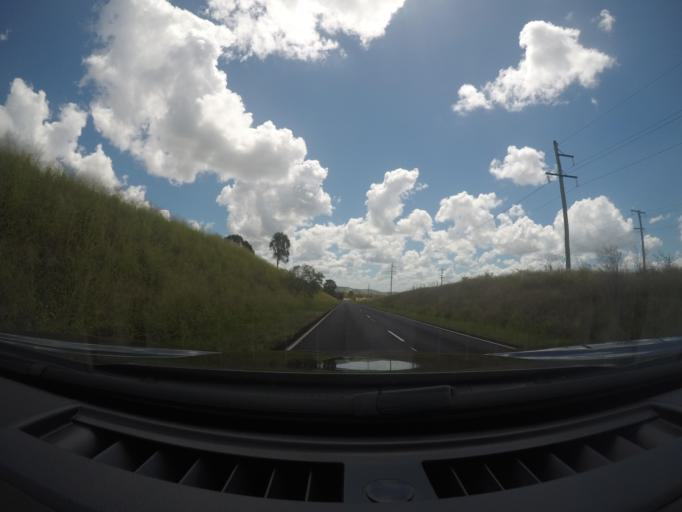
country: AU
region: Queensland
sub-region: Moreton Bay
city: Woodford
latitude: -27.1425
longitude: 152.4932
